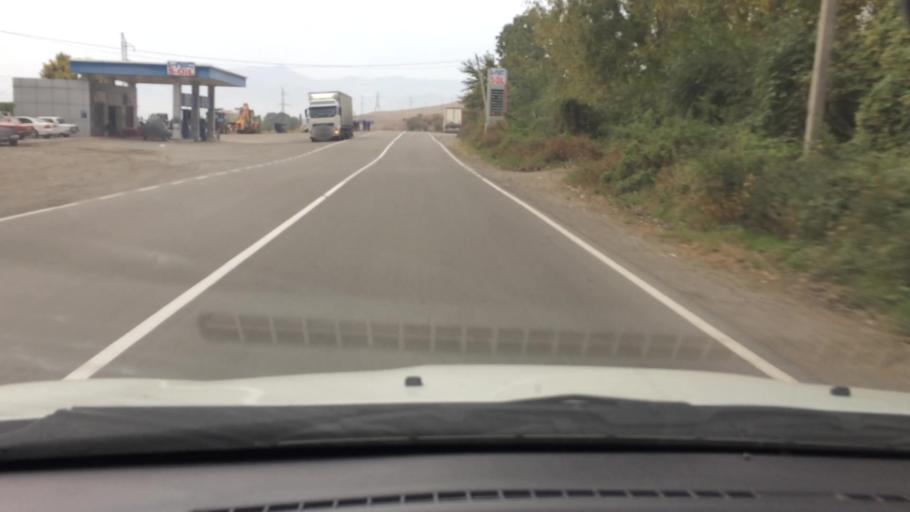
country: AM
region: Tavush
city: Bagratashen
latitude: 41.2927
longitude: 44.7879
